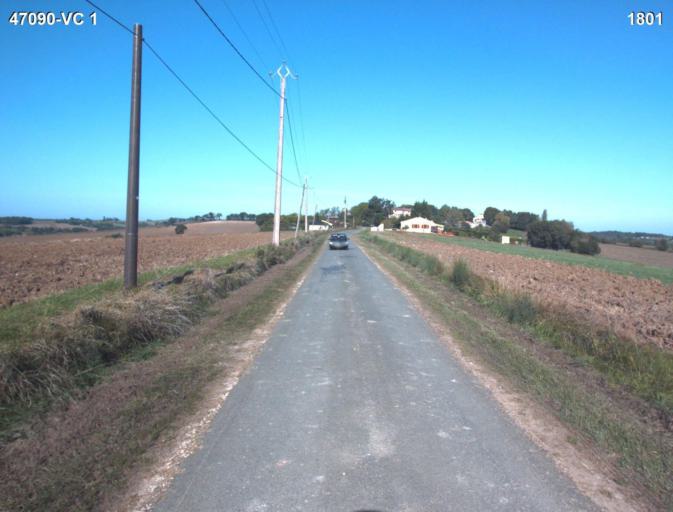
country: FR
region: Aquitaine
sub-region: Departement du Lot-et-Garonne
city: Nerac
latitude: 44.1604
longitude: 0.3879
